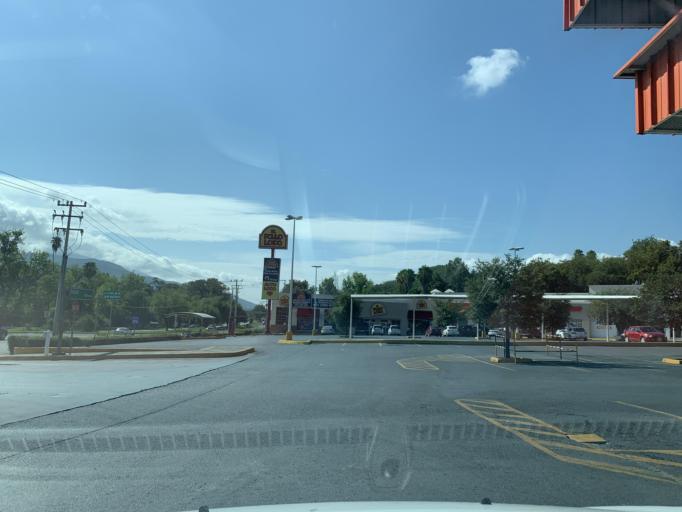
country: MX
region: Nuevo Leon
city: Santiago
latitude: 25.4250
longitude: -100.1485
